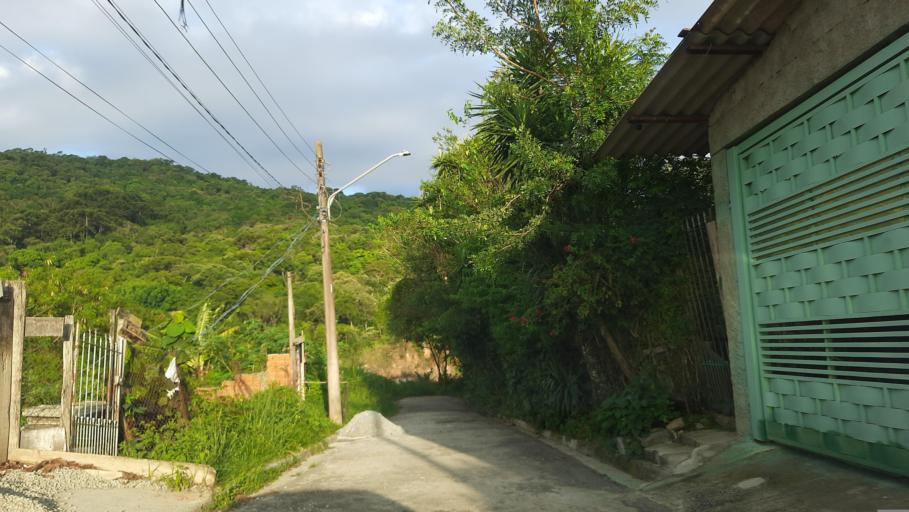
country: BR
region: Sao Paulo
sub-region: Caieiras
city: Caieiras
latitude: -23.4345
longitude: -46.7085
